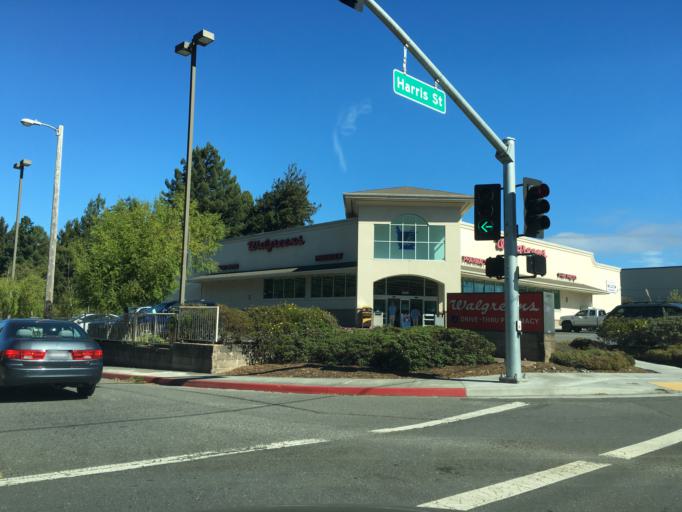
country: US
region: California
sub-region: Humboldt County
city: Cutten
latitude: 40.7805
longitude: -124.1396
